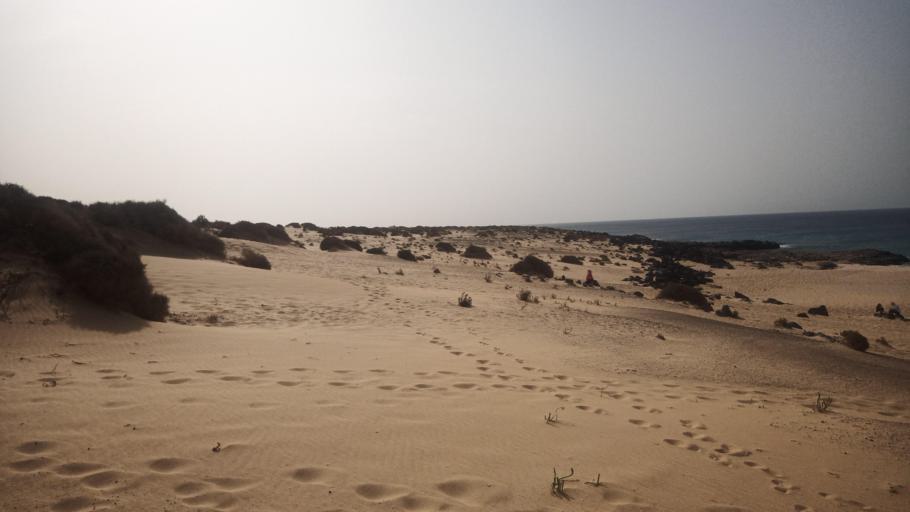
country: ES
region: Canary Islands
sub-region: Provincia de Las Palmas
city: Haria
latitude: 29.2743
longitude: -13.5156
